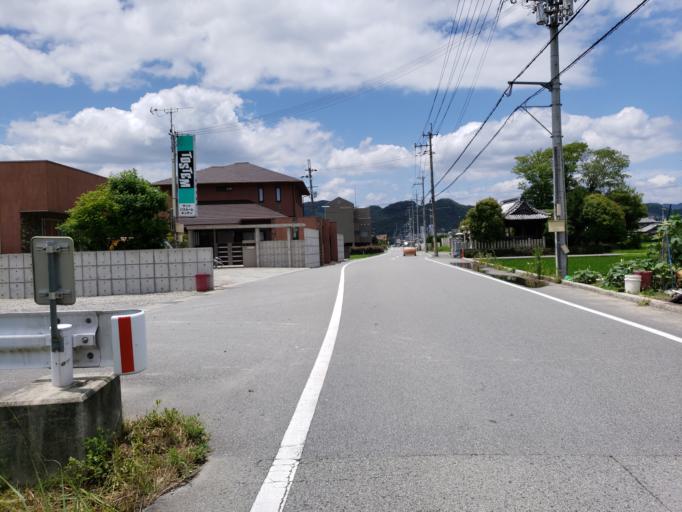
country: JP
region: Hyogo
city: Himeji
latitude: 34.8834
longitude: 134.7400
